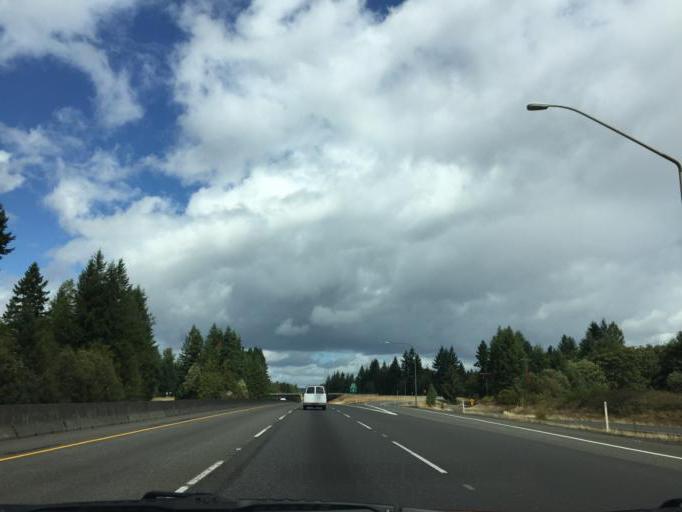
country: US
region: Washington
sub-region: Lewis County
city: Winlock
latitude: 46.4360
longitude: -122.8890
